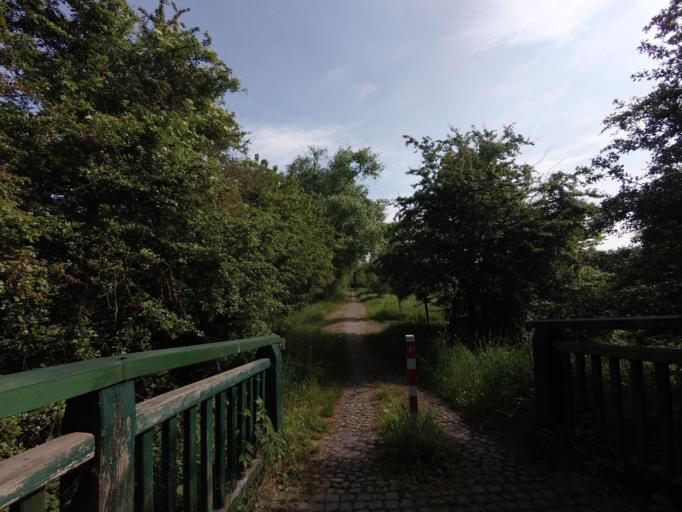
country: DE
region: Lower Saxony
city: Braunschweig
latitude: 52.3146
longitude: 10.5244
